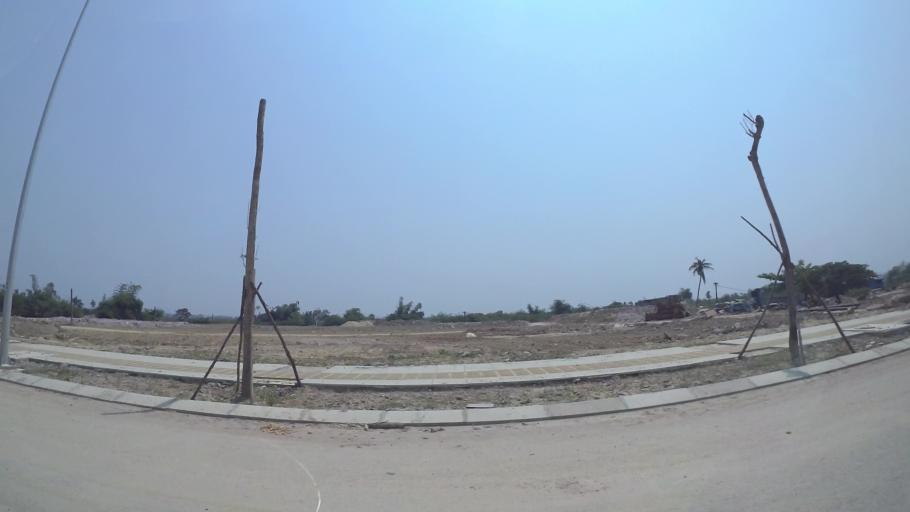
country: VN
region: Da Nang
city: Cam Le
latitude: 15.9979
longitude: 108.2240
